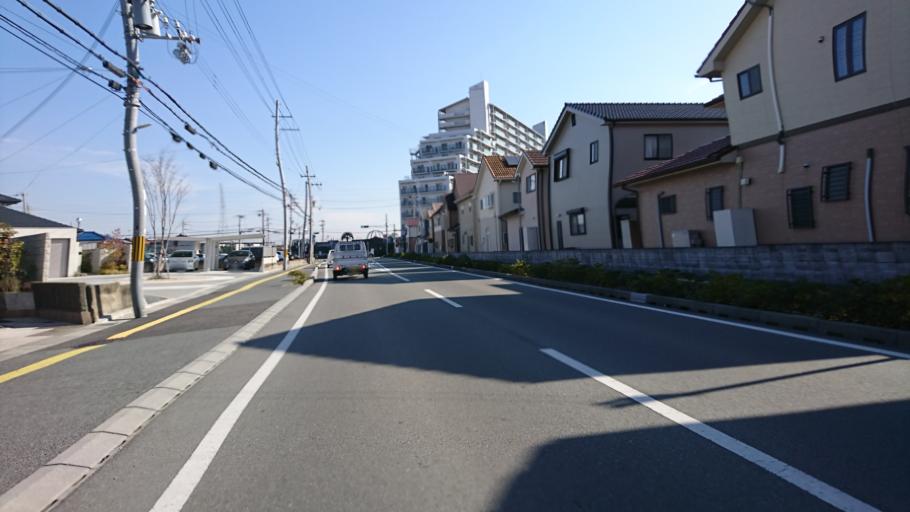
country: JP
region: Hyogo
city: Kakogawacho-honmachi
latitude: 34.7742
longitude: 134.8070
